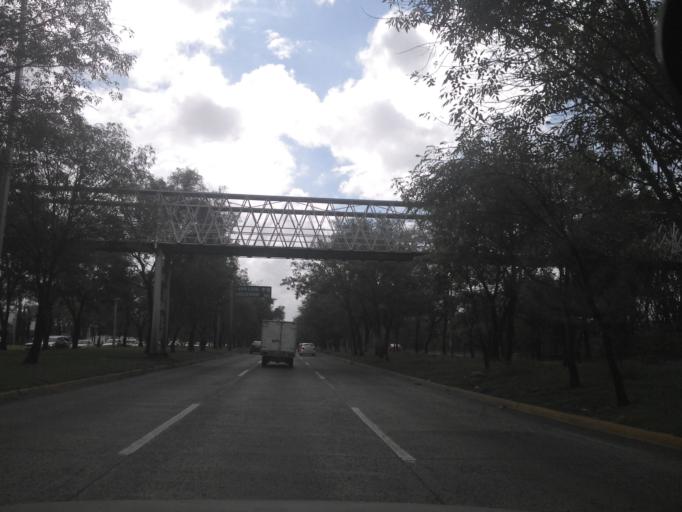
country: MX
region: Jalisco
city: Guadalajara
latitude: 20.6405
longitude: -103.3490
